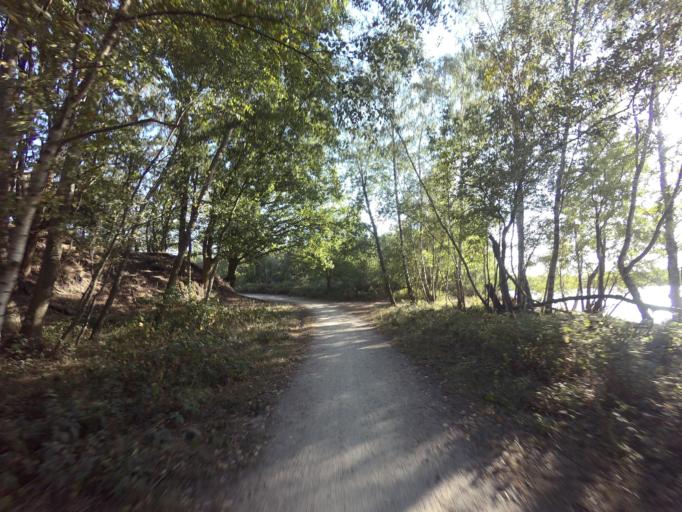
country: NL
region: North Brabant
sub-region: Gemeente Mill en Sint Hubert
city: Wilbertoord
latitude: 51.6960
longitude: 5.7507
